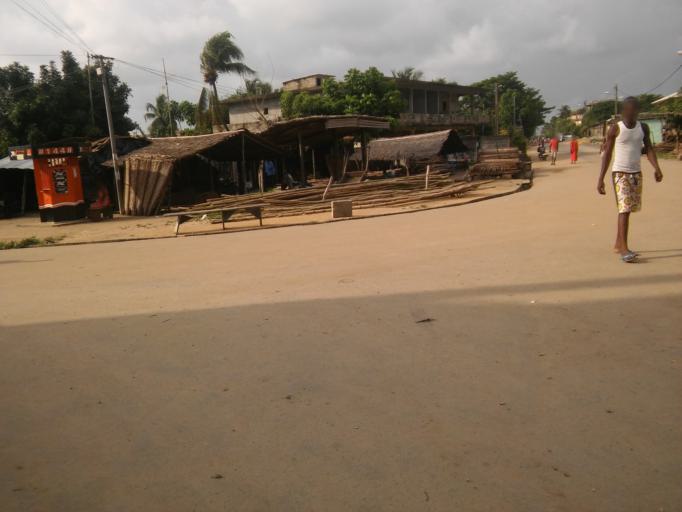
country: CI
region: Sud-Comoe
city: Grand-Bassam
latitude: 5.2099
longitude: -3.7313
